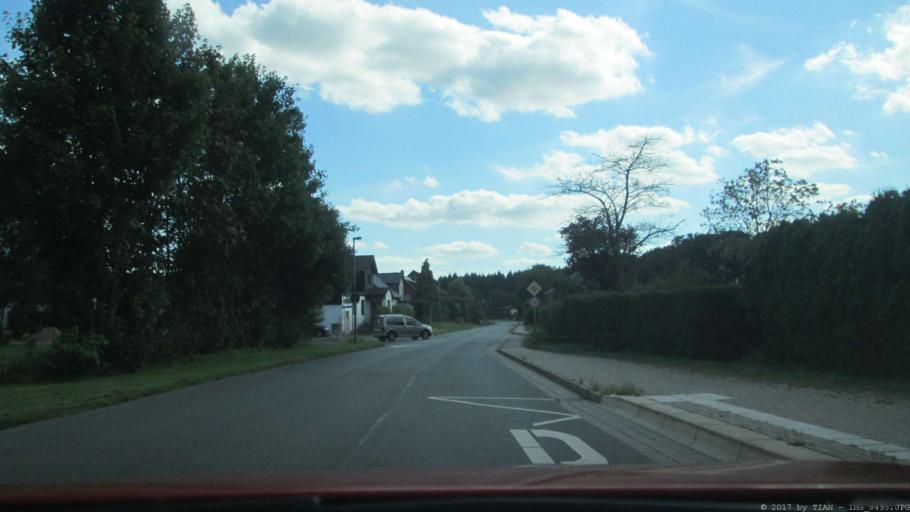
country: DE
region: Lower Saxony
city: Wolfsburg
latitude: 52.3825
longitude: 10.8027
